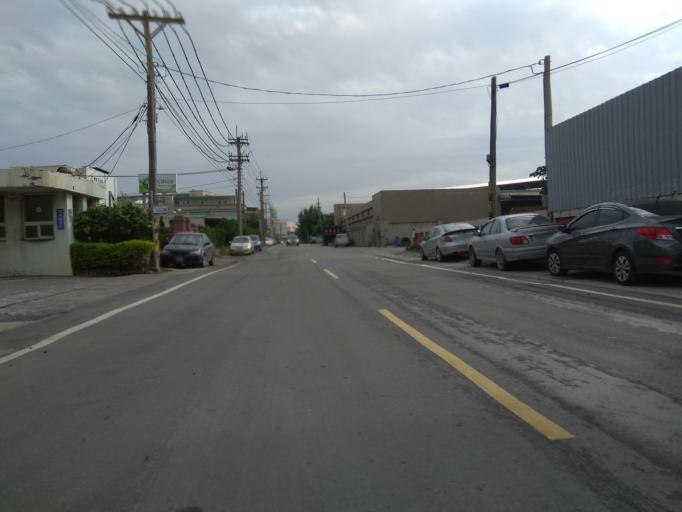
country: TW
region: Taiwan
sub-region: Hsinchu
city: Zhubei
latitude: 24.9860
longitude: 121.0296
